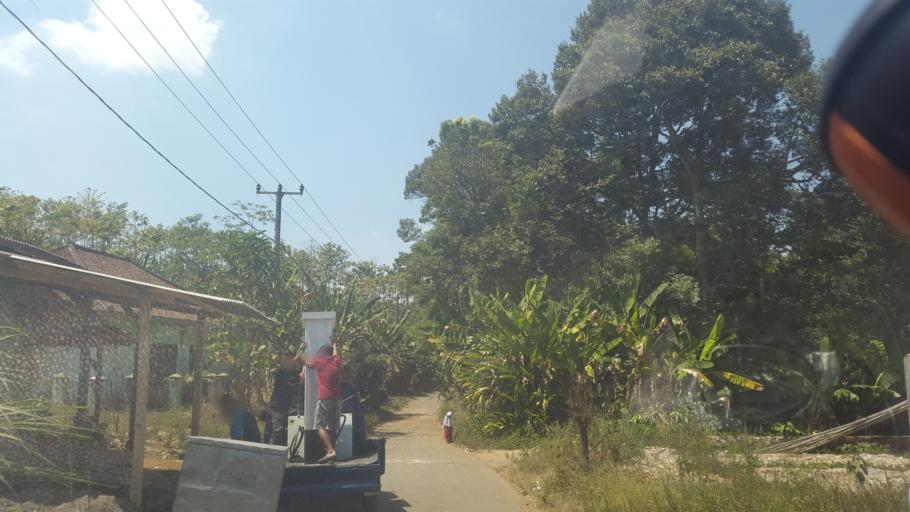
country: ID
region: West Java
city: Gunungkalong
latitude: -6.9174
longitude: 106.8037
